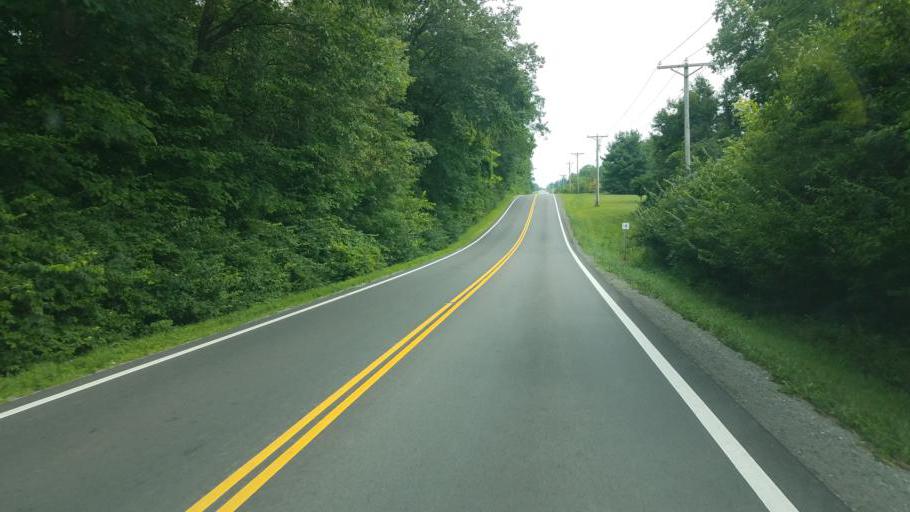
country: US
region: Ohio
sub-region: Marion County
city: Marion
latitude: 40.5166
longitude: -83.0595
